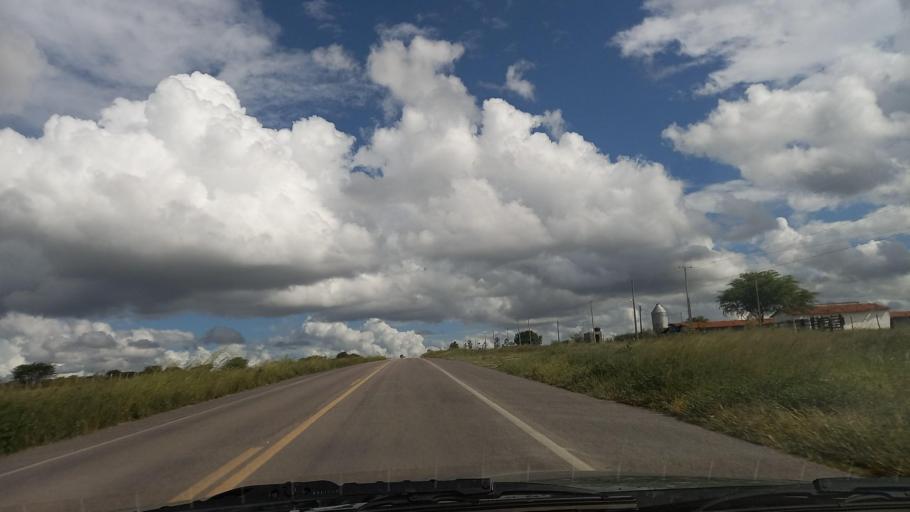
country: BR
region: Pernambuco
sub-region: Lajedo
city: Lajedo
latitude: -8.6258
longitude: -36.3020
